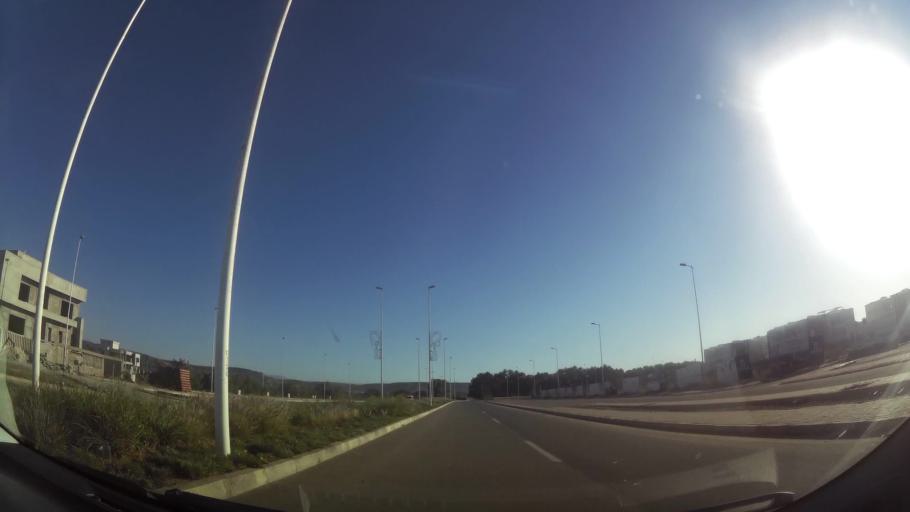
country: MA
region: Oriental
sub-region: Berkane-Taourirt
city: Madagh
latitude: 35.0928
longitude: -2.2607
